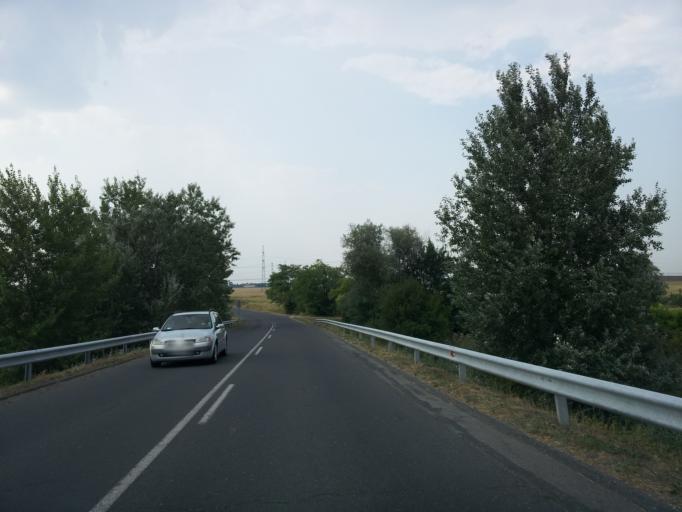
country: HU
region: Gyor-Moson-Sopron
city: Toltestava
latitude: 47.6416
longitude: 17.6914
